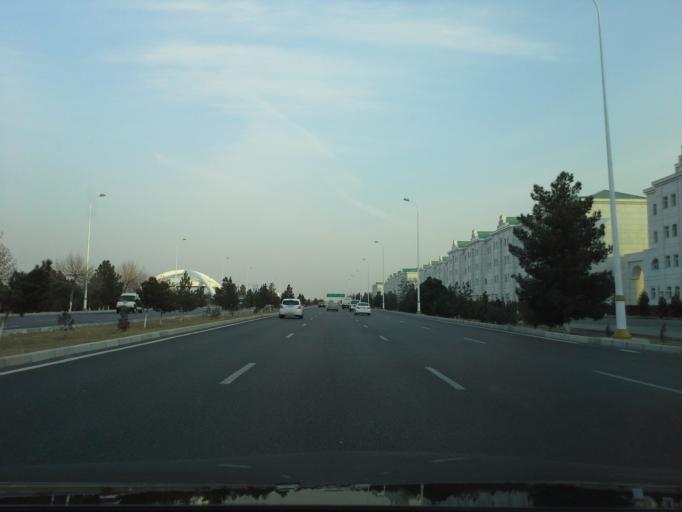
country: TM
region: Ahal
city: Ashgabat
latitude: 37.9895
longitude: 58.3207
